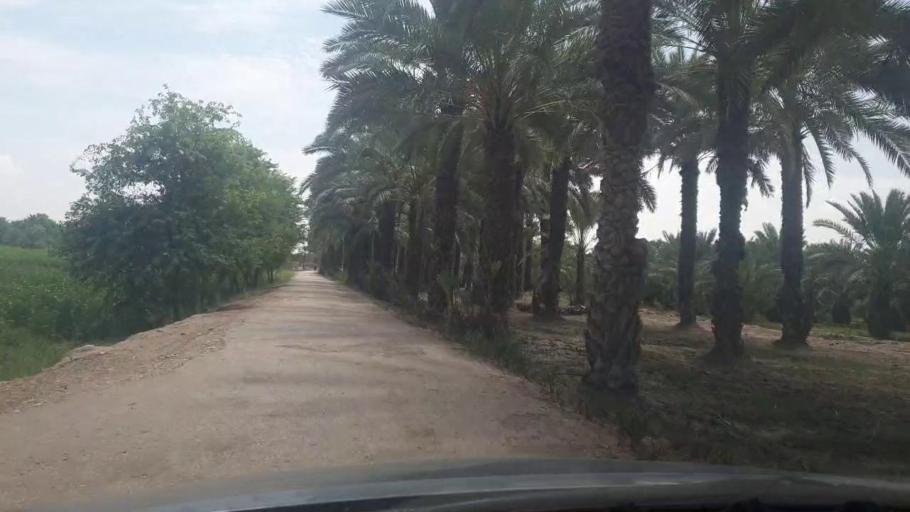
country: PK
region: Sindh
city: Kot Diji
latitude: 27.3978
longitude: 68.7583
